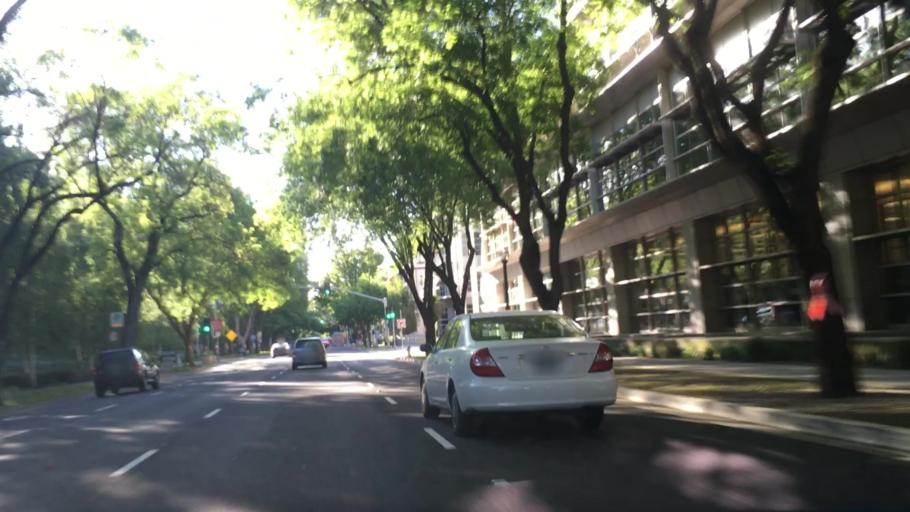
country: US
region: California
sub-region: Sacramento County
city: Sacramento
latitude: 38.5750
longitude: -121.5057
